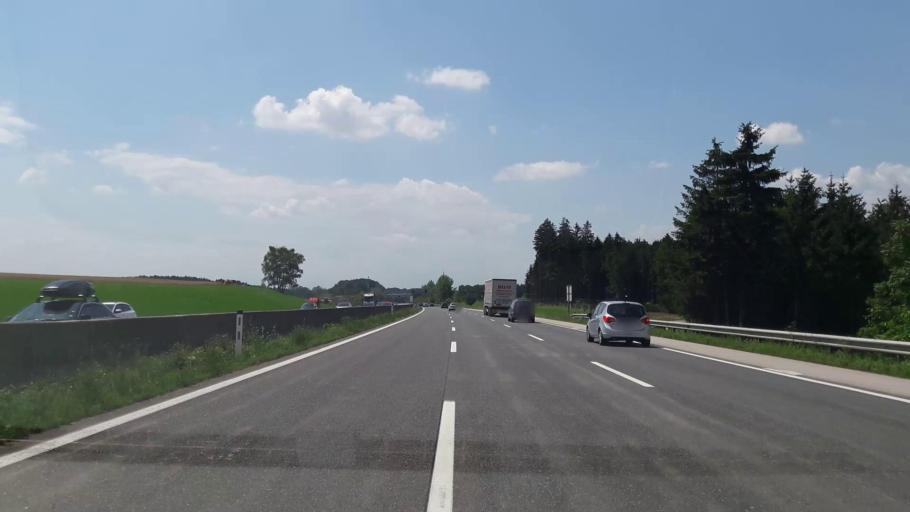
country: AT
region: Lower Austria
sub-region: Politischer Bezirk Amstetten
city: Wolfsbach
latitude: 48.1144
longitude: 14.7093
